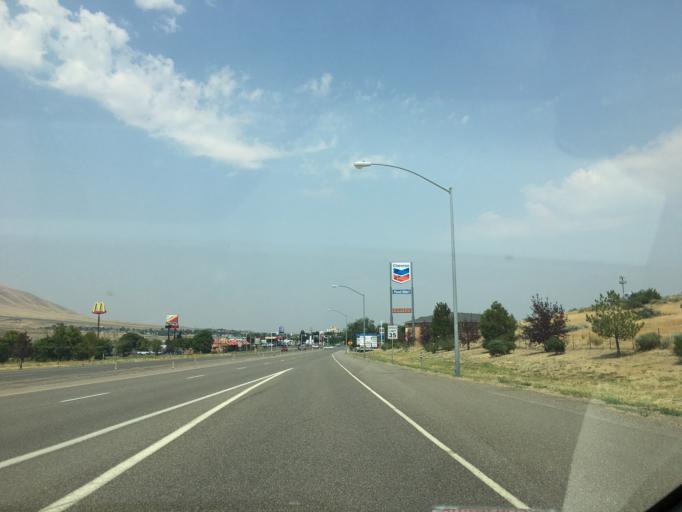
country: US
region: Nevada
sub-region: Humboldt County
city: Winnemucca
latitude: 40.9565
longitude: -117.7491
